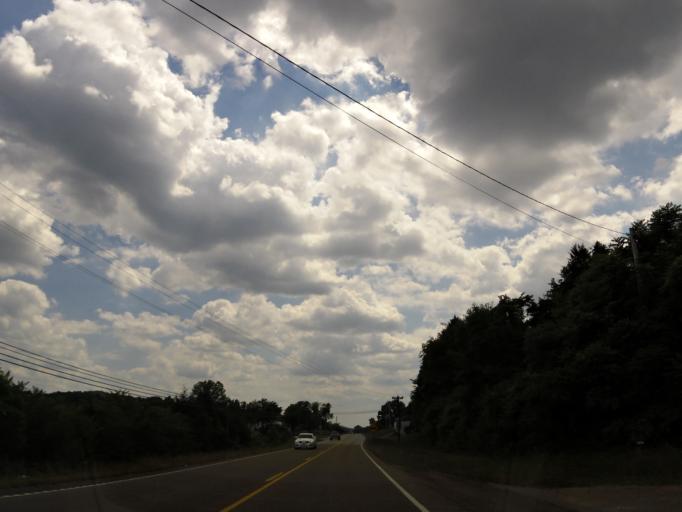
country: US
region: Tennessee
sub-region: Bledsoe County
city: Pikeville
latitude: 35.5122
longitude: -85.2826
